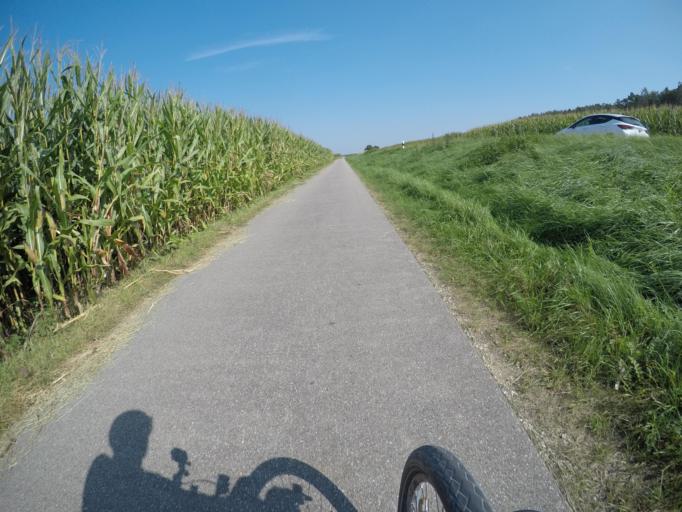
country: DE
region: Bavaria
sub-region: Swabia
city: Zusamaltheim
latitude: 48.5479
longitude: 10.6193
